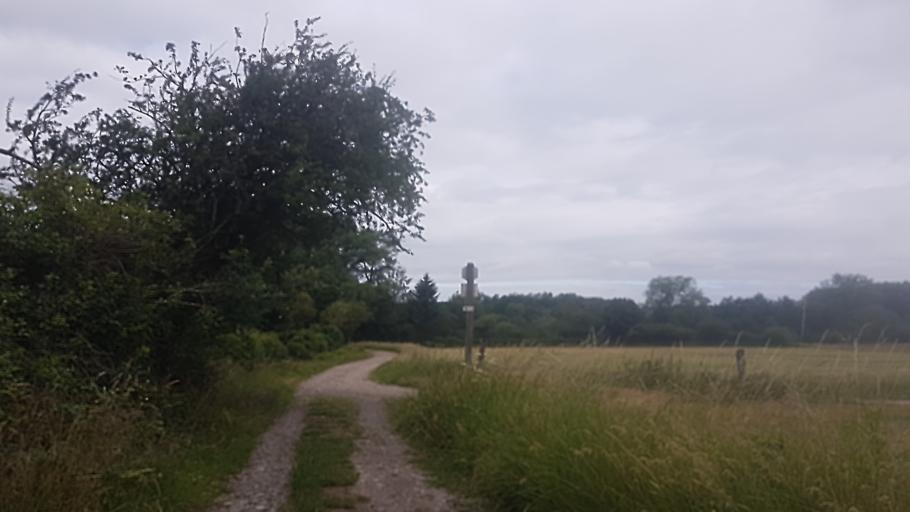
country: BE
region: Wallonia
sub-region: Province de Namur
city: Couvin
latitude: 50.0914
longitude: 4.5424
